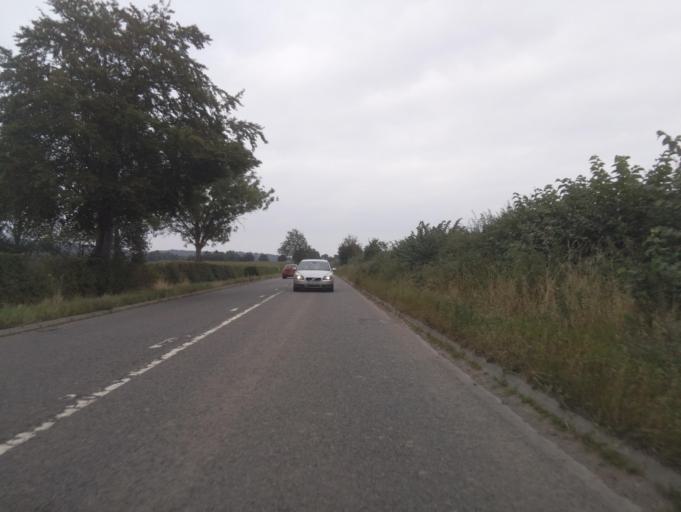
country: GB
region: England
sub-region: Shropshire
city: Shawbury
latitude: 52.8233
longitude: -2.6054
